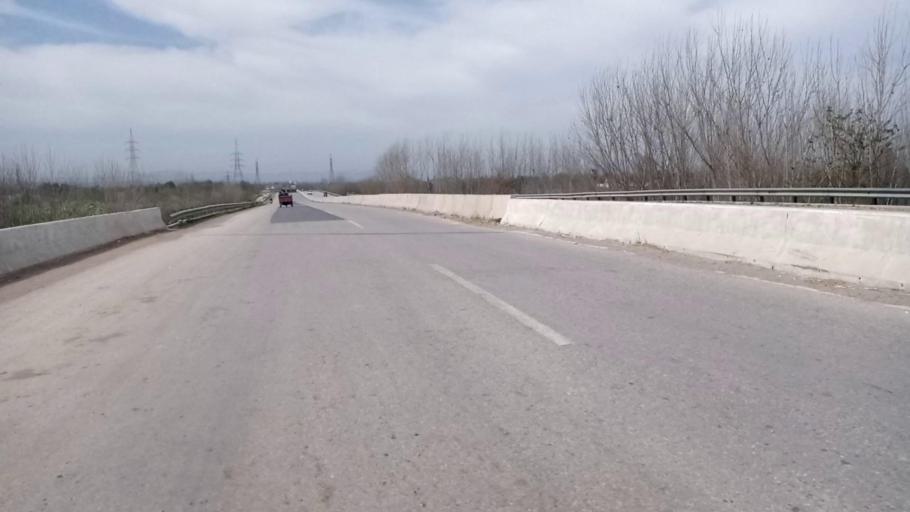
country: PK
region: Khyber Pakhtunkhwa
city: Peshawar
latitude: 34.0603
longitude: 71.6070
